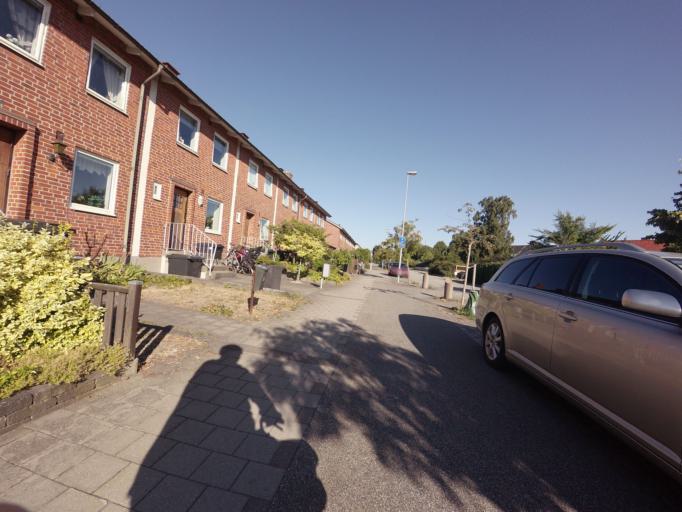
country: SE
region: Skane
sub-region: Trelleborgs Kommun
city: Trelleborg
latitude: 55.3812
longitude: 13.1442
